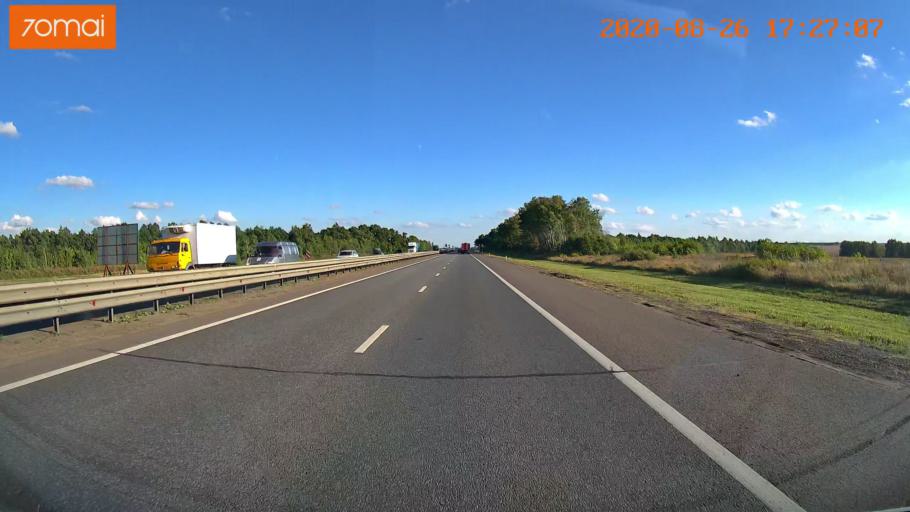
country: RU
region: Tula
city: Kazachka
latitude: 53.4771
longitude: 38.1223
